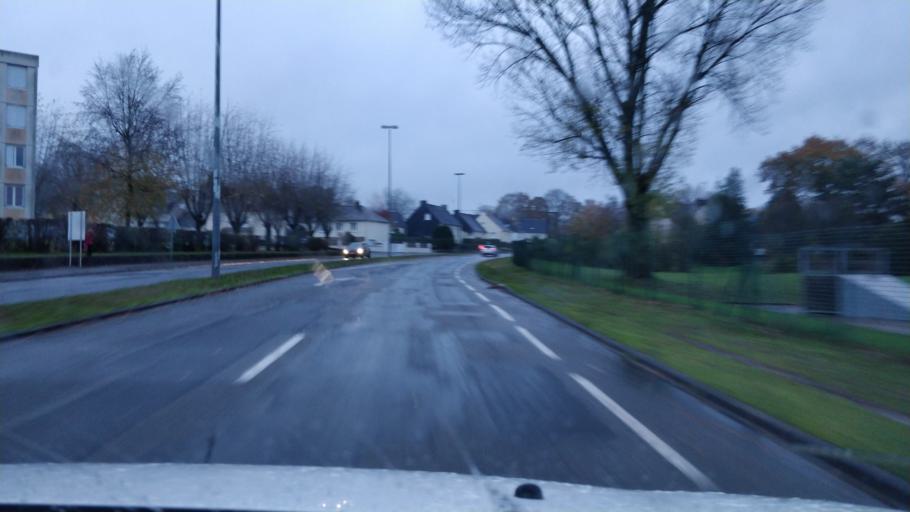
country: FR
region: Brittany
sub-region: Departement des Cotes-d'Armor
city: Loudeac
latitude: 48.1791
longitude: -2.7496
